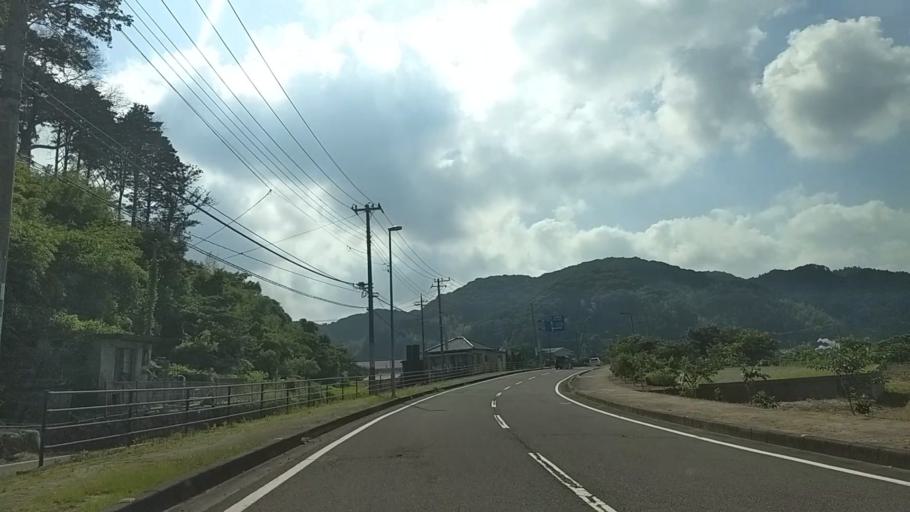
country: JP
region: Shizuoka
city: Shimoda
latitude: 34.6487
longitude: 138.8597
